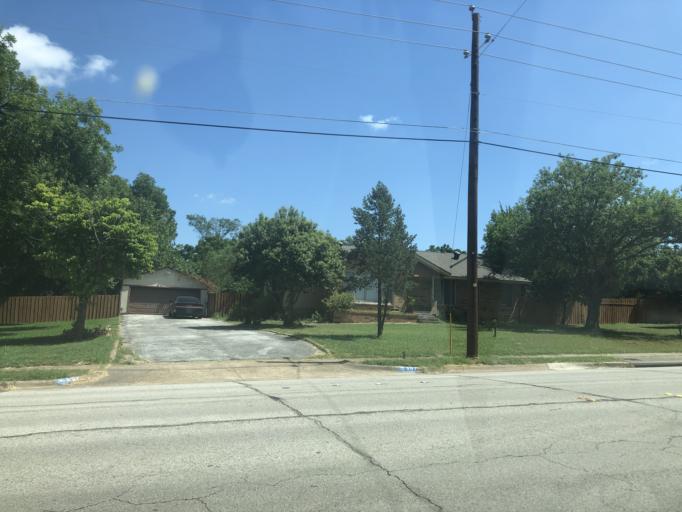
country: US
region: Texas
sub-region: Dallas County
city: Duncanville
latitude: 32.6515
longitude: -96.9190
